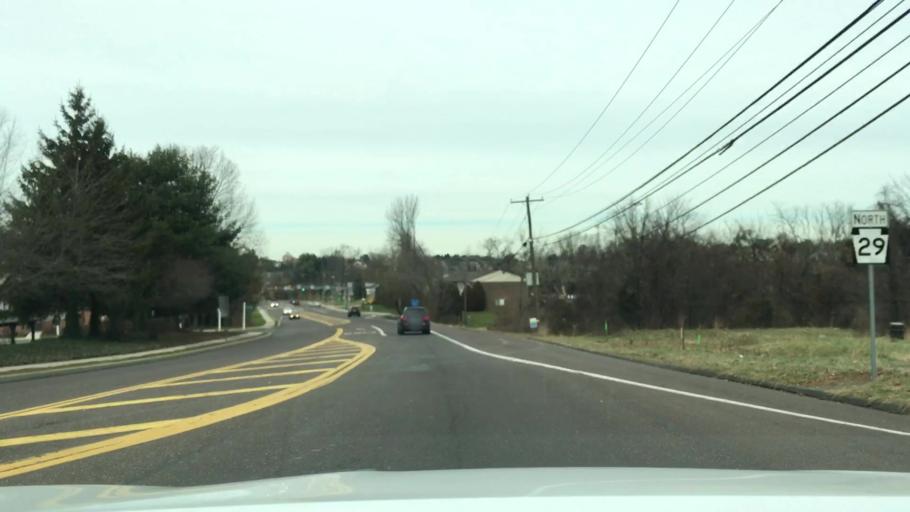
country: US
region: Pennsylvania
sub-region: Lehigh County
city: Emmaus
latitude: 40.5289
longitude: -75.5077
